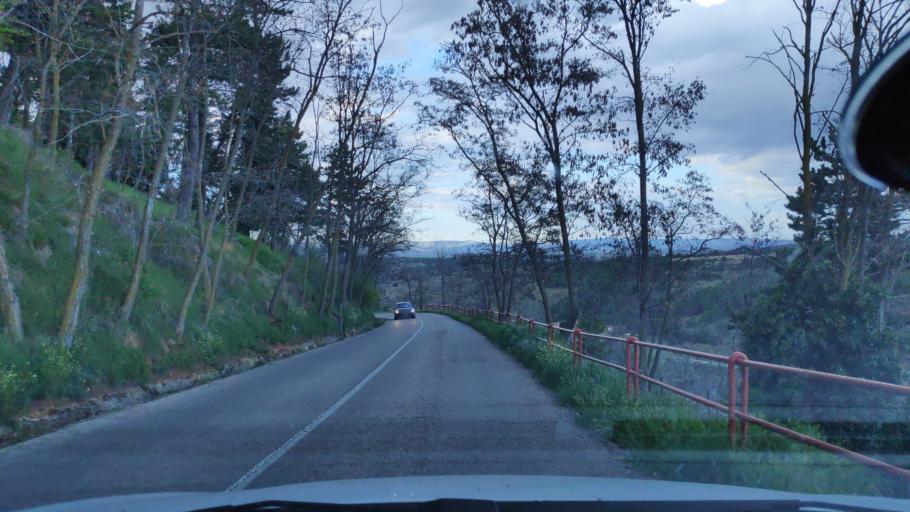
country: ES
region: Castille and Leon
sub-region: Provincia de Soria
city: Soria
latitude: 41.7607
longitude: -2.4573
